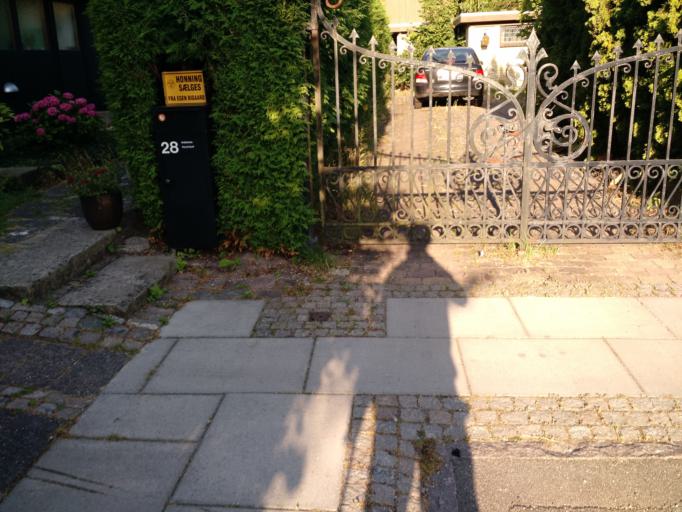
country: DK
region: Capital Region
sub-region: Herlev Kommune
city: Herlev
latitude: 55.7536
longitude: 12.4235
